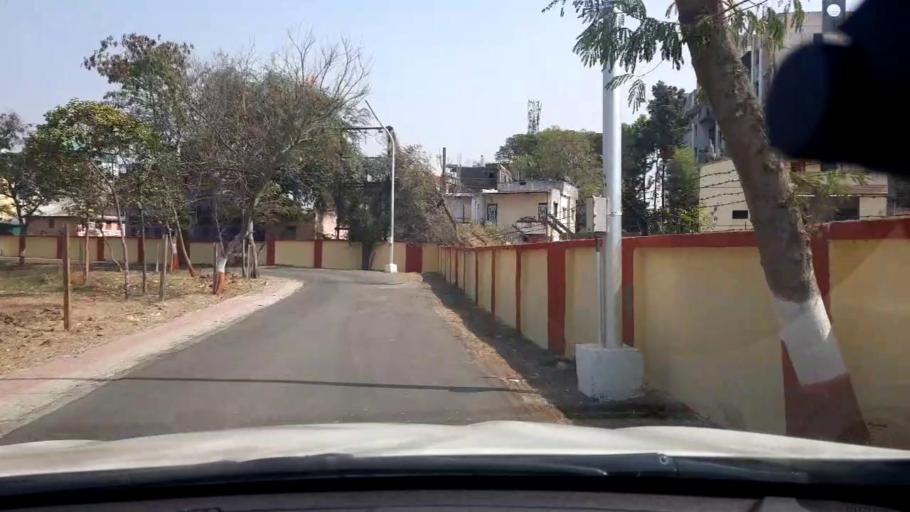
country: IN
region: Maharashtra
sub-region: Pune Division
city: Shivaji Nagar
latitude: 18.5418
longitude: 73.8640
